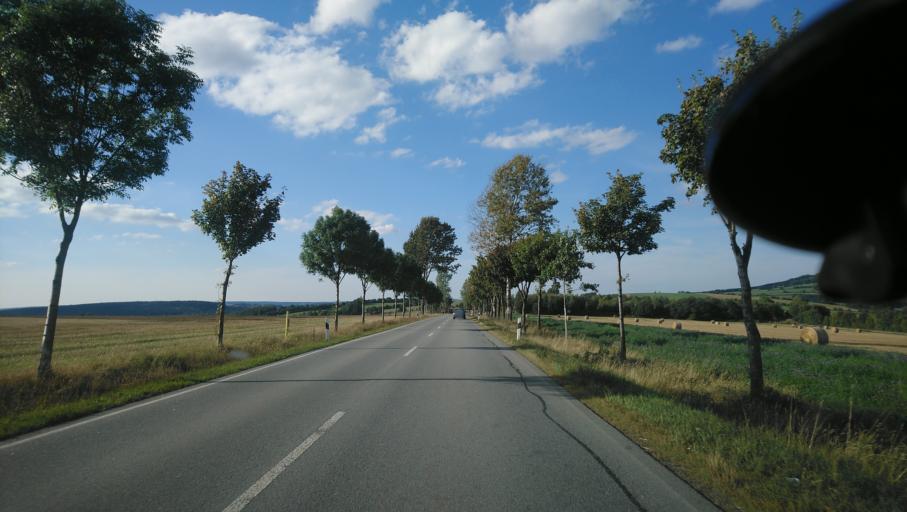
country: DE
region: Saxony
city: Konigswalde
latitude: 50.5439
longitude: 13.0203
